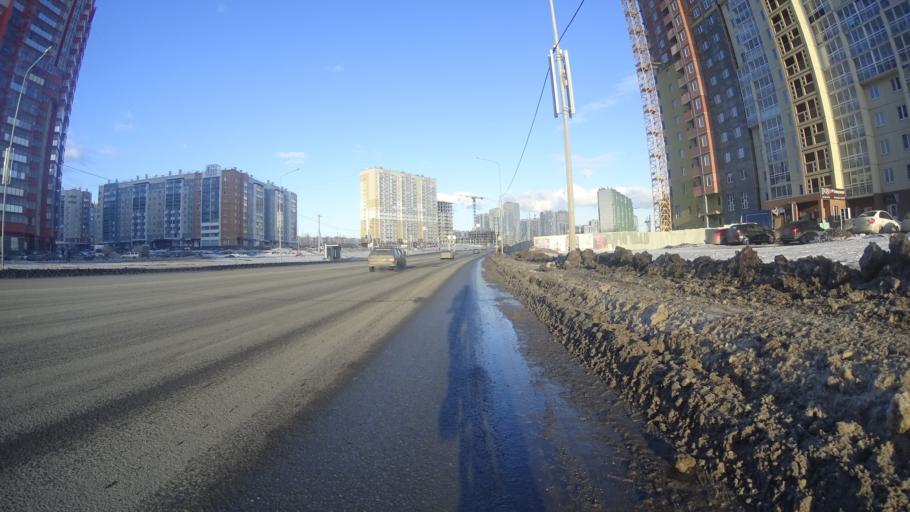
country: RU
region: Chelyabinsk
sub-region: Gorod Chelyabinsk
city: Chelyabinsk
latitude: 55.1728
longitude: 61.3152
